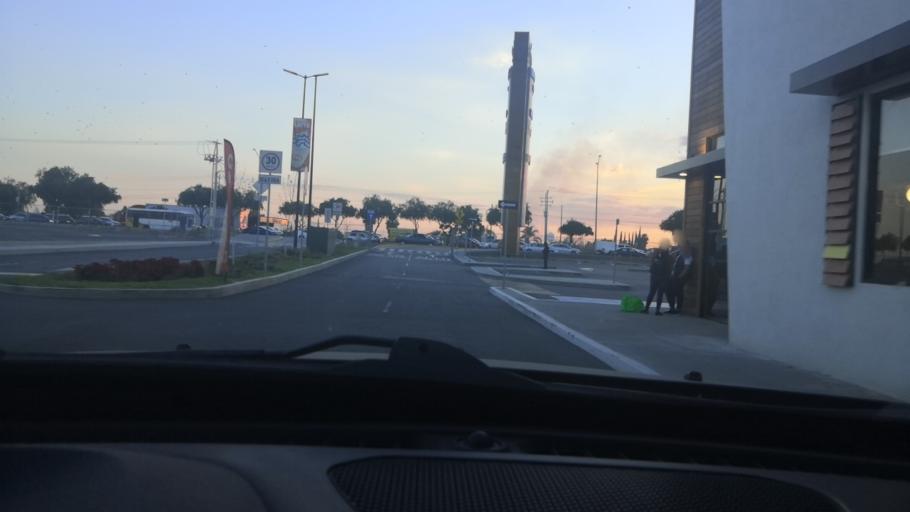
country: MX
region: Guanajuato
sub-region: Leon
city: Fraccionamiento Paraiso Real
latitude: 21.0791
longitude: -101.6053
